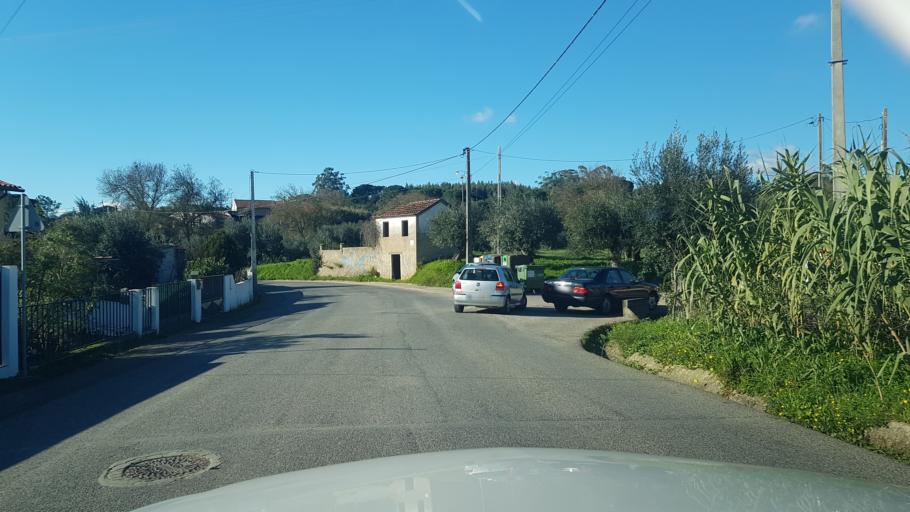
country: PT
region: Santarem
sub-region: Entroncamento
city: Entroncamento
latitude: 39.4778
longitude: -8.4998
